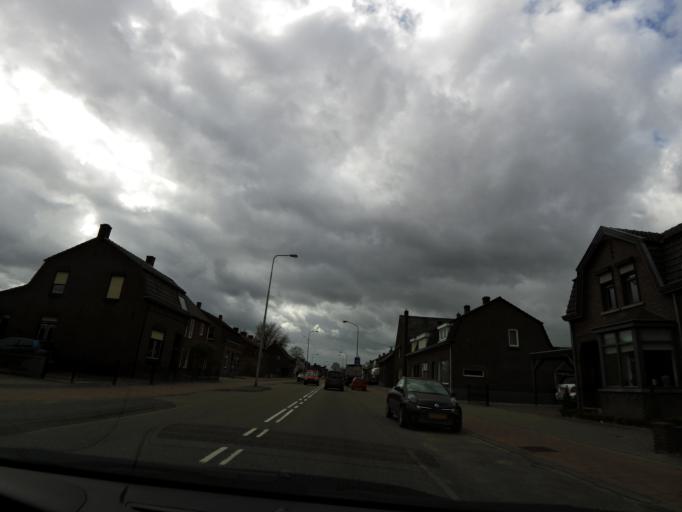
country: NL
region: Limburg
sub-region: Gemeente Beesel
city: Reuver
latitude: 51.2900
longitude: 6.0827
